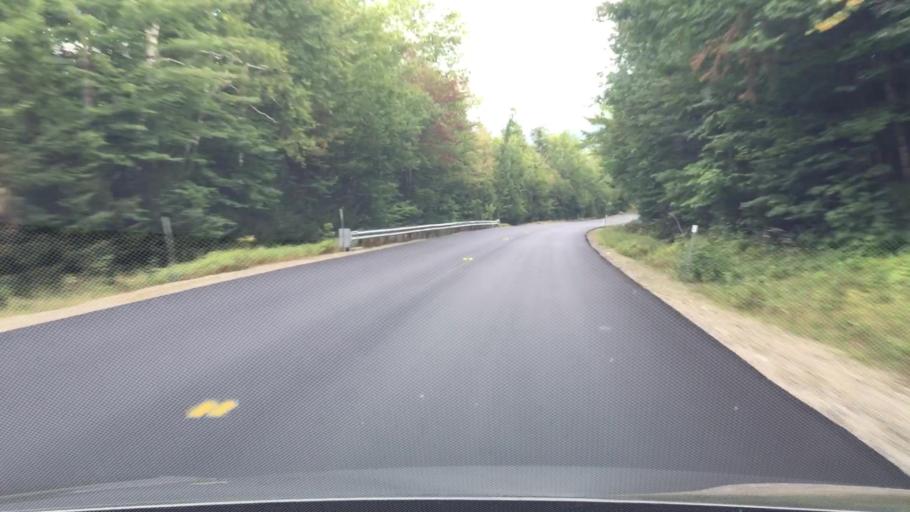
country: US
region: New Hampshire
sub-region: Carroll County
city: Sandwich
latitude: 44.0213
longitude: -71.4382
